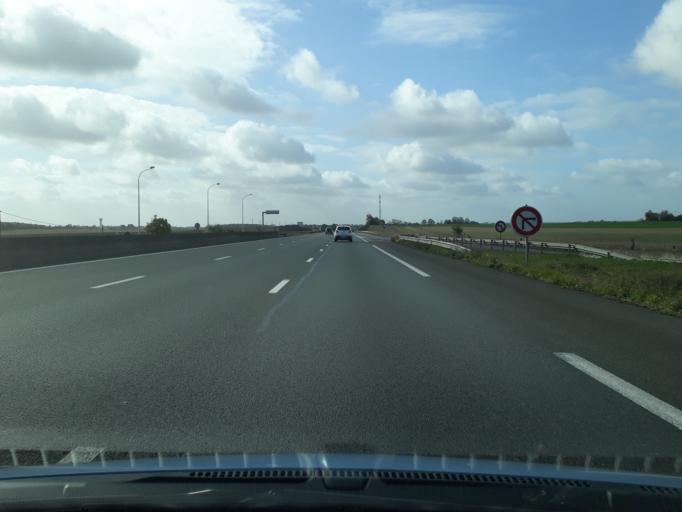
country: FR
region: Centre
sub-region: Departement du Loir-et-Cher
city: La Chaussee-Saint-Victor
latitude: 47.6626
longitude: 1.3856
